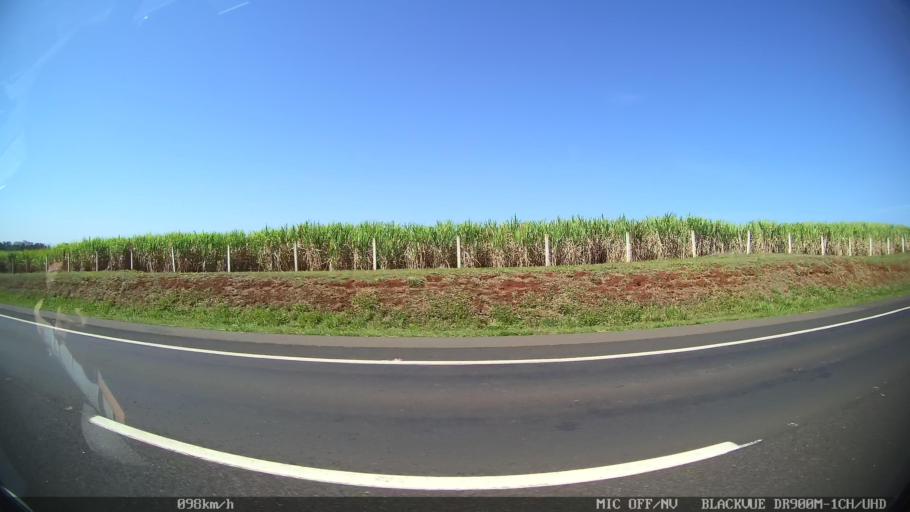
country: BR
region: Sao Paulo
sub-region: Batatais
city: Batatais
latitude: -20.7915
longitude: -47.5607
